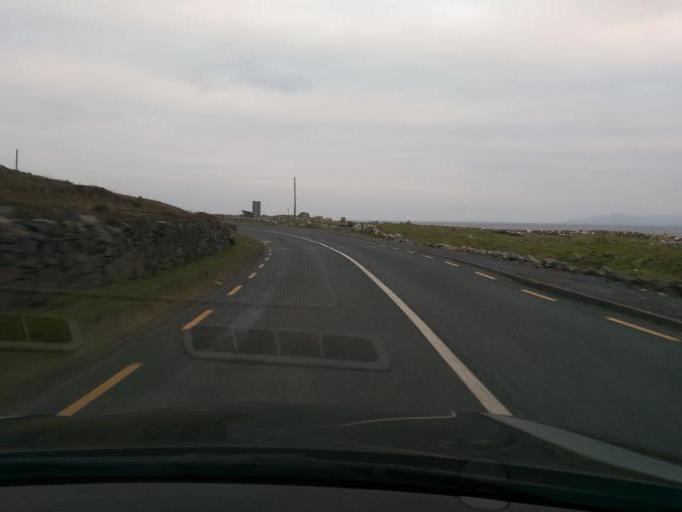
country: IE
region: Connaught
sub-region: County Galway
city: Bearna
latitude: 53.2476
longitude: -9.1843
